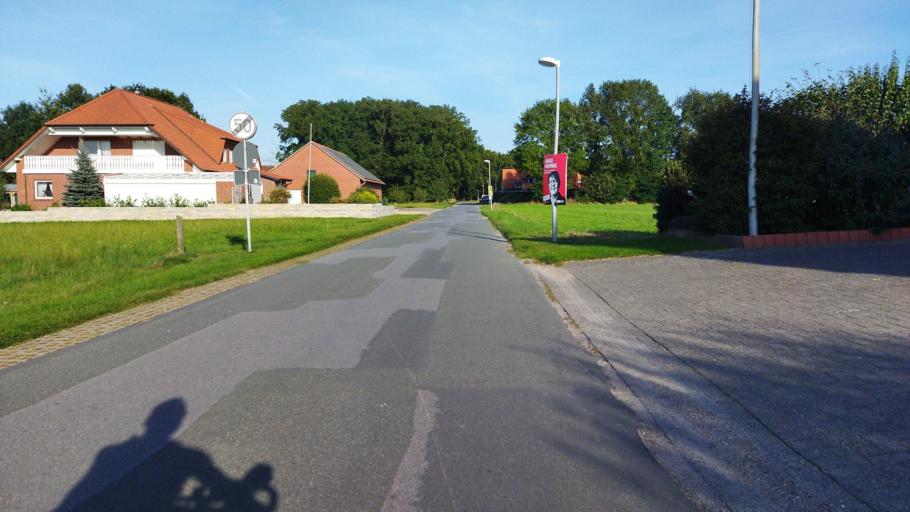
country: DE
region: Lower Saxony
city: Bad Laer
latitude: 52.0993
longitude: 8.0642
